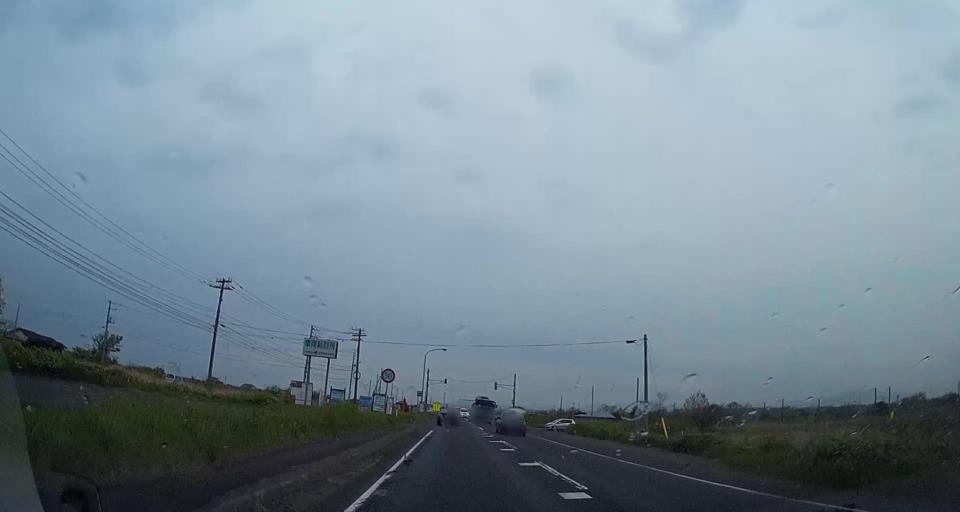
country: JP
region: Hokkaido
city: Shiraoi
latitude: 42.5804
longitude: 141.4248
